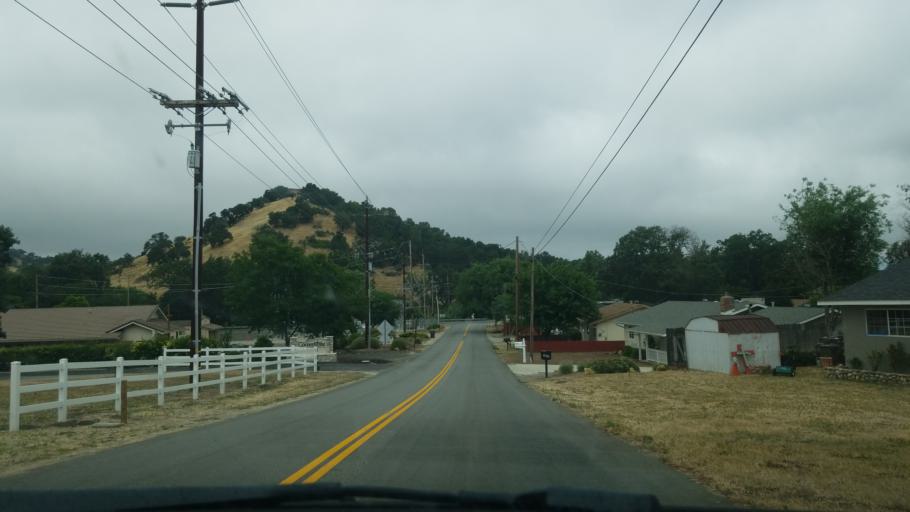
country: US
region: California
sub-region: San Luis Obispo County
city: Atascadero
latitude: 35.4648
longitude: -120.6701
